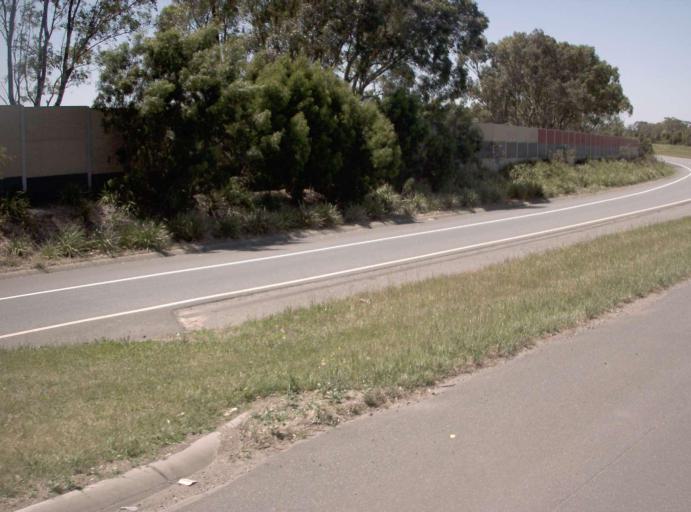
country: AU
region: Victoria
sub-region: Casey
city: Berwick
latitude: -38.0590
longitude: 145.3670
